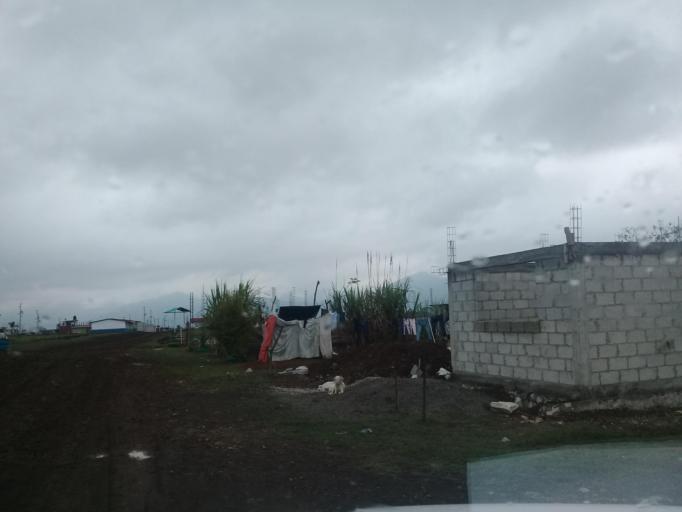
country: MX
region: Veracruz
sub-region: Cordoba
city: San Jose de Tapia
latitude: 18.8549
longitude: -96.9596
